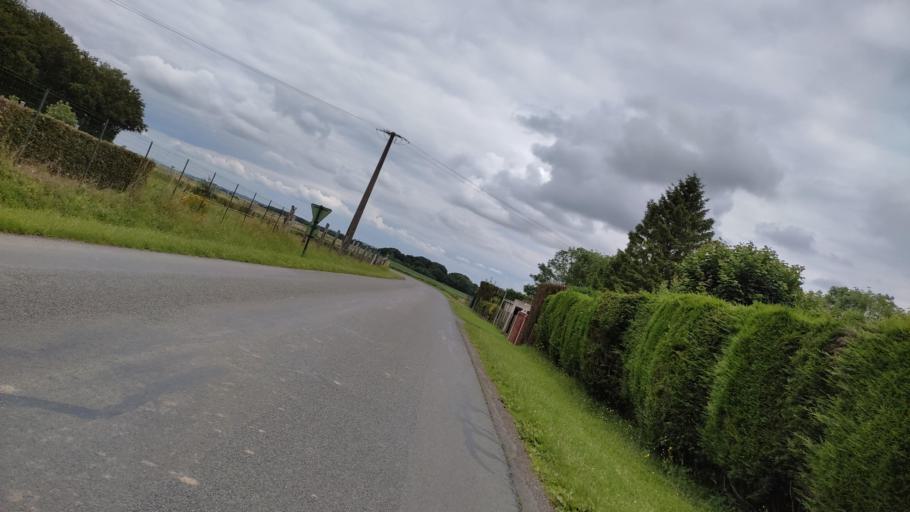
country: FR
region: Nord-Pas-de-Calais
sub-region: Departement du Pas-de-Calais
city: Beaumetz-les-Loges
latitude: 50.2387
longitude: 2.6659
